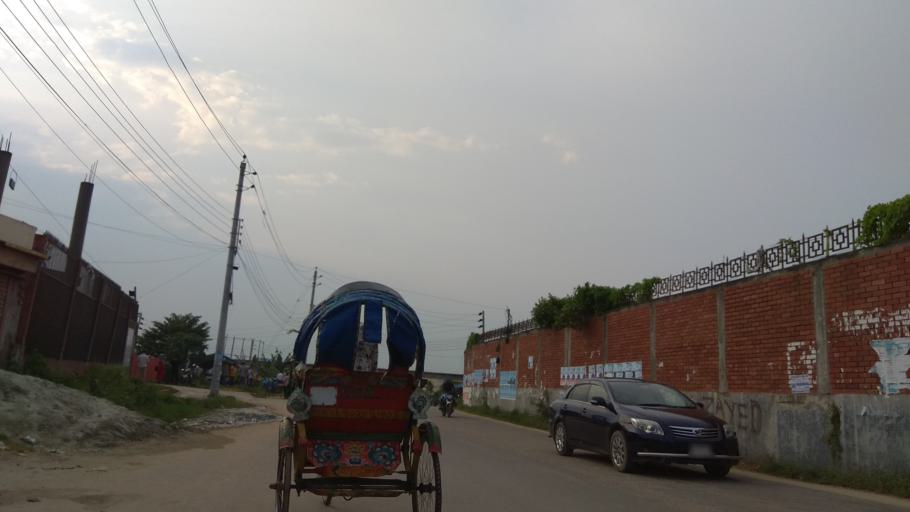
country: BD
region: Dhaka
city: Tungi
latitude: 23.8562
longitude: 90.3857
